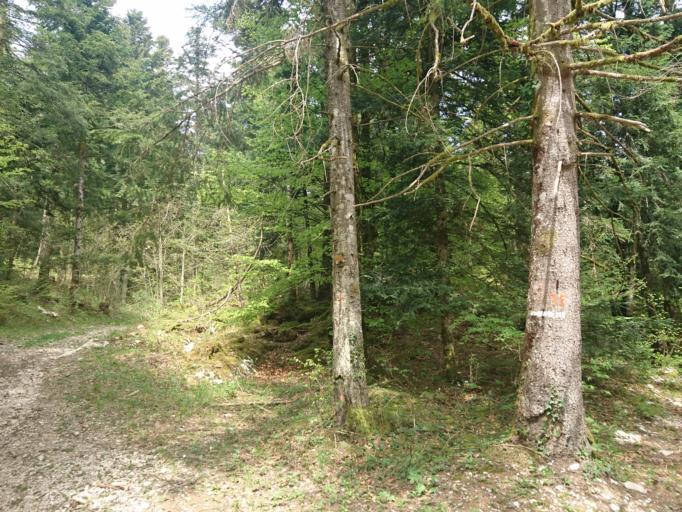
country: FR
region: Rhone-Alpes
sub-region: Departement de l'Ain
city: Nantua
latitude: 46.1685
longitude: 5.6553
